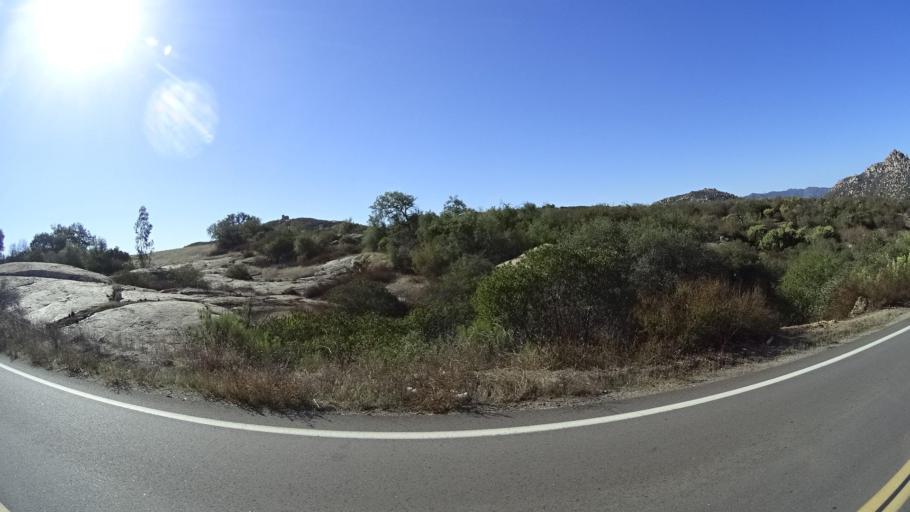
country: US
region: California
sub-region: San Diego County
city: Jamul
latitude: 32.6761
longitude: -116.7363
